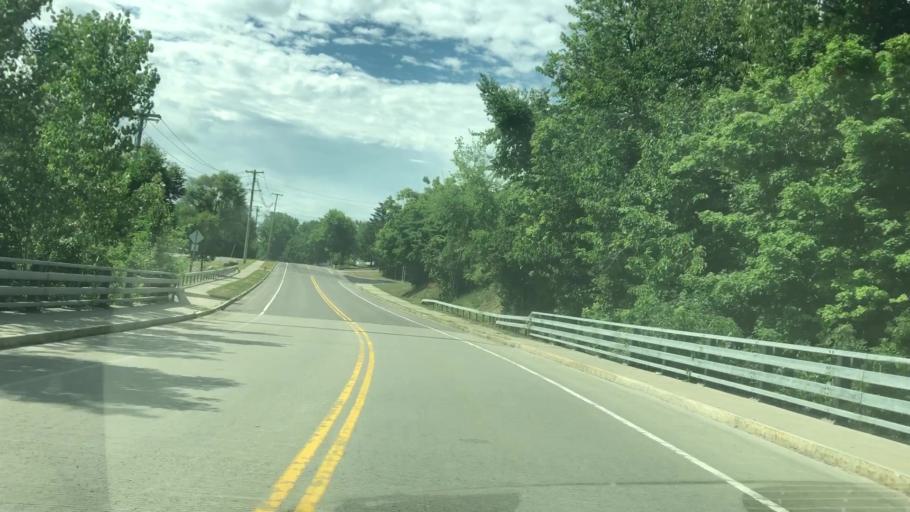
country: US
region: New York
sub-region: Monroe County
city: Fairport
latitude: 43.0867
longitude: -77.4021
